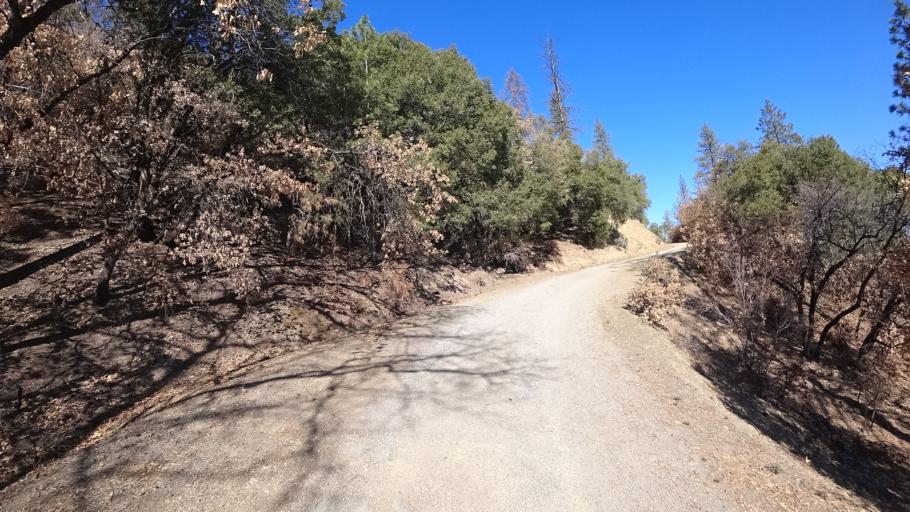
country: US
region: California
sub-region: Tehama County
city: Rancho Tehama Reserve
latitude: 39.6766
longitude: -122.7040
